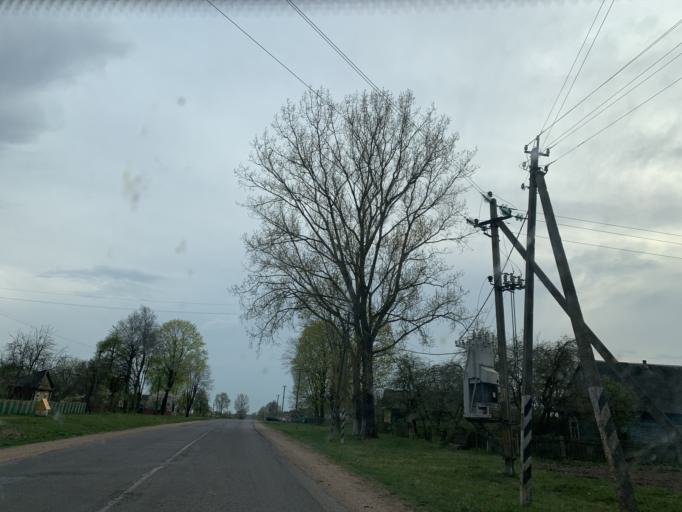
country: BY
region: Minsk
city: Kapyl'
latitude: 53.2747
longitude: 26.9686
